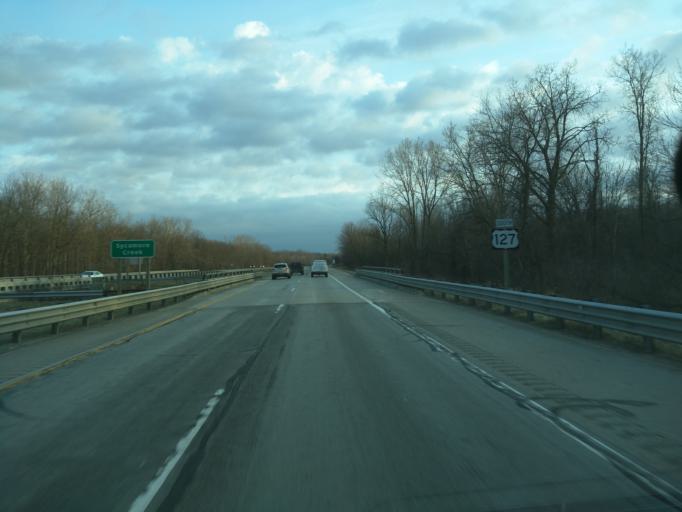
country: US
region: Michigan
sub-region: Ingham County
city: Holt
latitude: 42.6331
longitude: -84.4770
